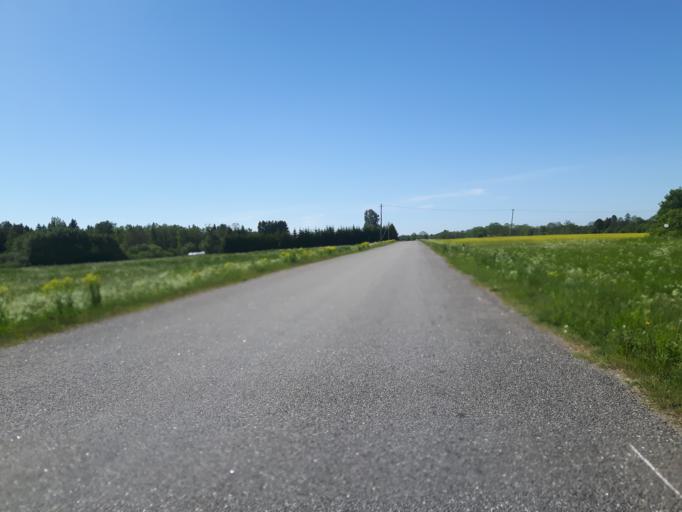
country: EE
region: Laeaene-Virumaa
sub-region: Haljala vald
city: Haljala
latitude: 59.5423
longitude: 26.2216
